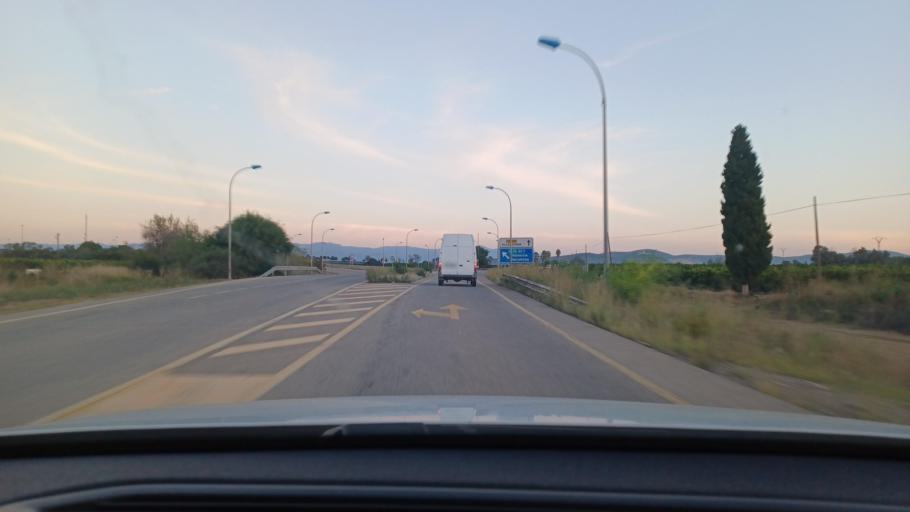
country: ES
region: Catalonia
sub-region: Provincia de Tarragona
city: Ulldecona
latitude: 40.5522
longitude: 0.4325
